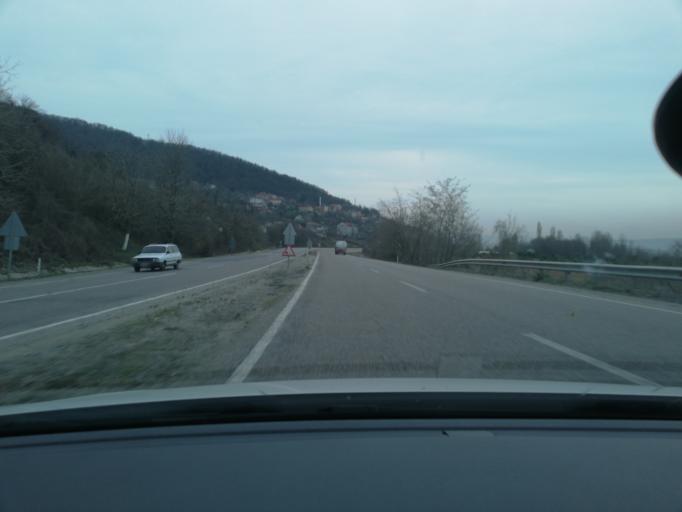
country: TR
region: Zonguldak
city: Caycuma
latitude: 41.4647
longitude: 32.0926
